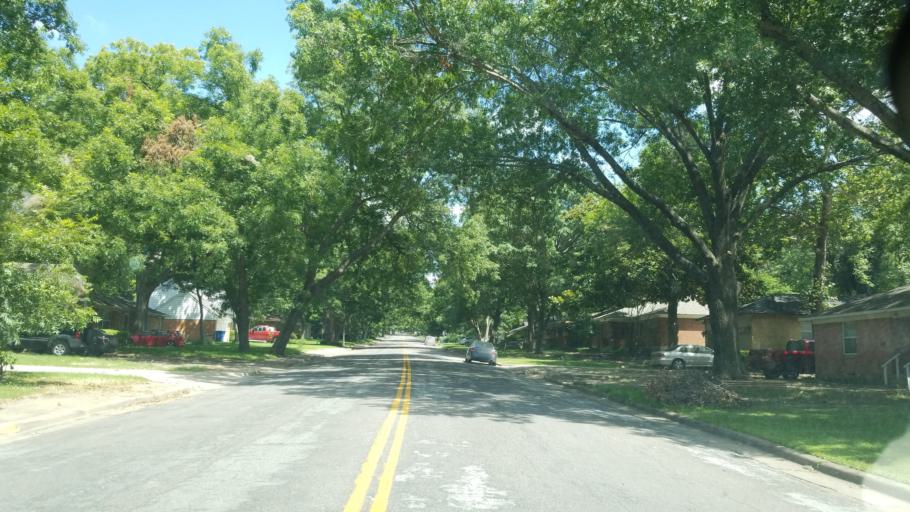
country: US
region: Texas
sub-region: Dallas County
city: Balch Springs
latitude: 32.7600
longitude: -96.6987
